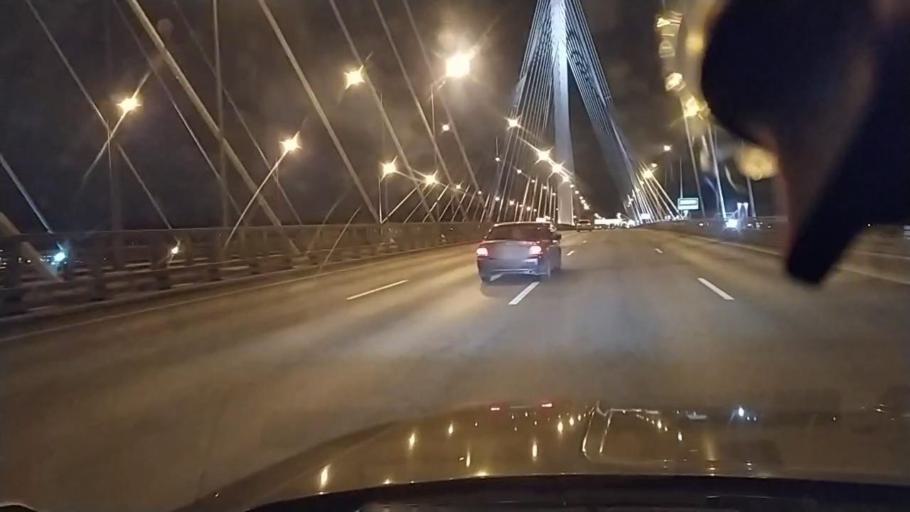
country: RU
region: St.-Petersburg
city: Staraya Derevnya
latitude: 59.9674
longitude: 30.2161
